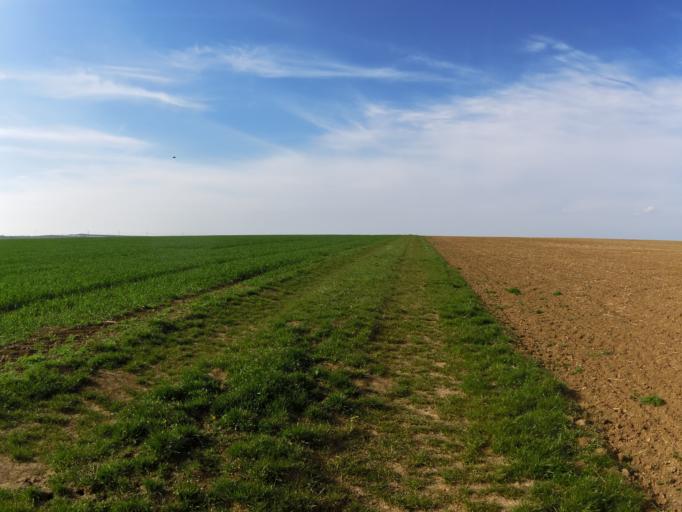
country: DE
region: Bavaria
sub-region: Regierungsbezirk Unterfranken
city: Mainstockheim
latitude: 49.7910
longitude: 10.1272
